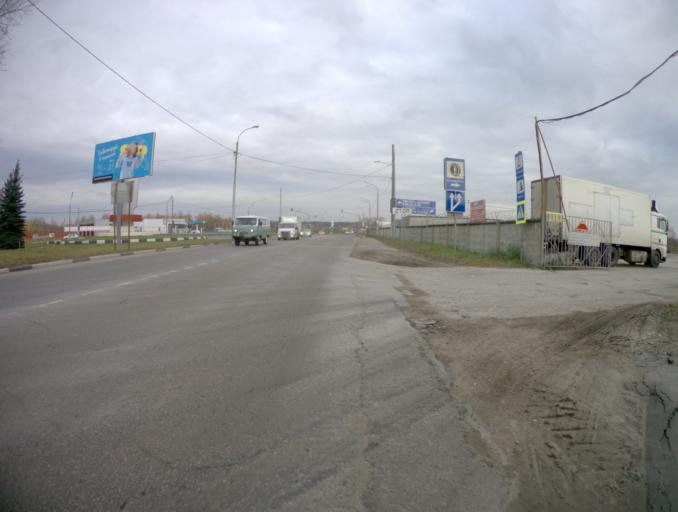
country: RU
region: Moskovskaya
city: Orekhovo-Zuyevo
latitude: 55.8368
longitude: 38.9721
